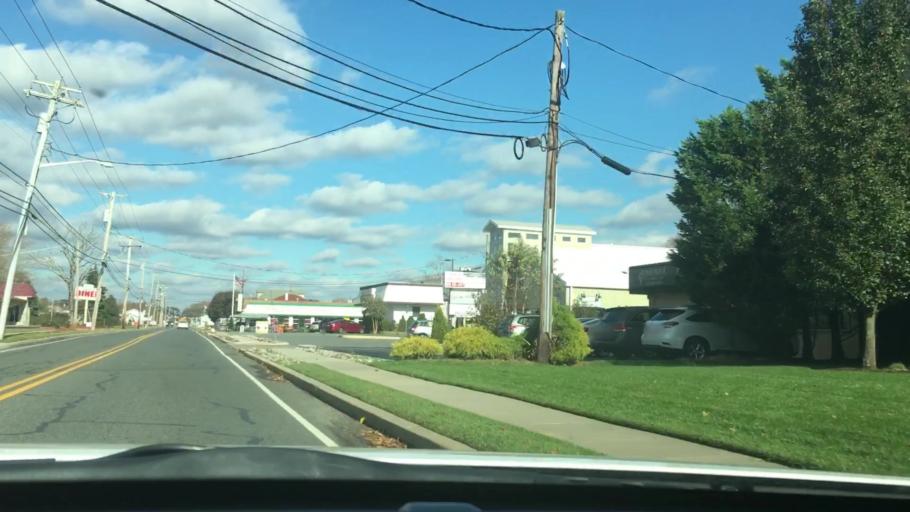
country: US
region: New Jersey
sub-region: Atlantic County
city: Northfield
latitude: 39.3712
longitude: -74.5574
